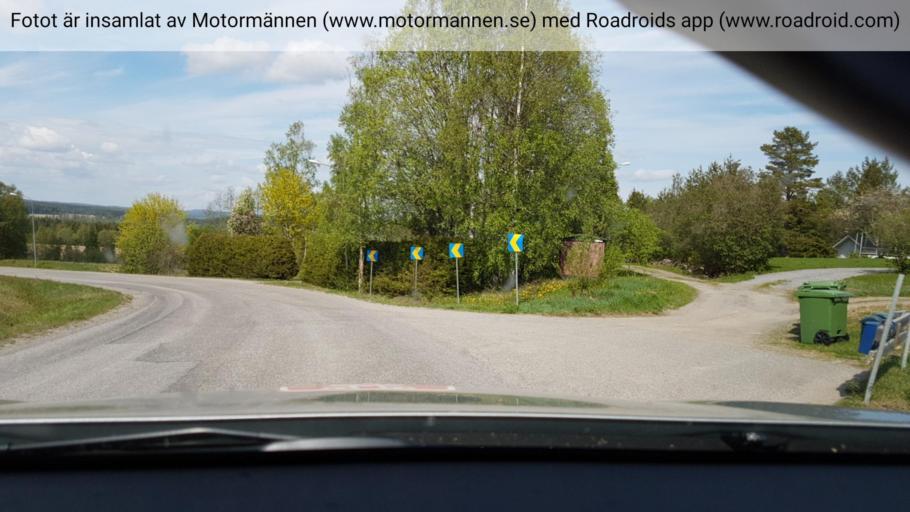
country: SE
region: Vaesterbotten
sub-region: Umea Kommun
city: Roback
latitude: 63.8716
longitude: 20.0461
